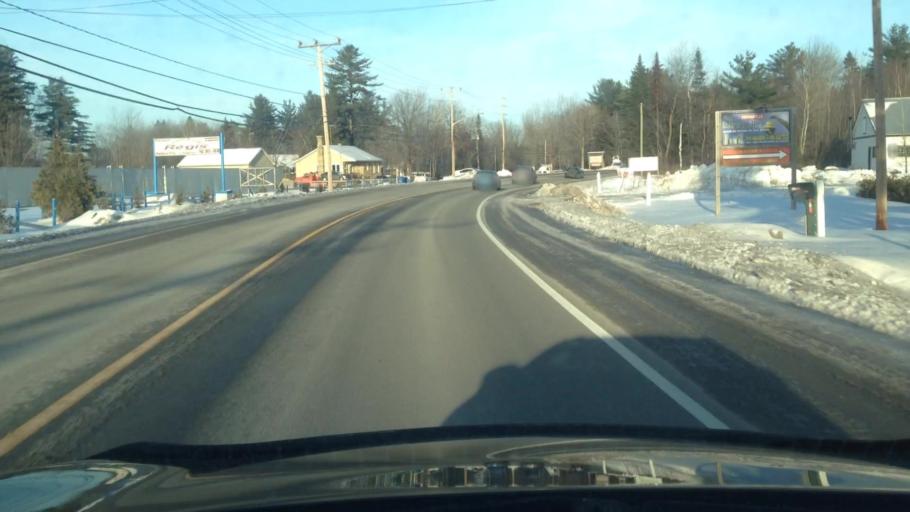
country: CA
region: Quebec
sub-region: Laurentides
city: Sainte-Sophie
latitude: 45.8146
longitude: -73.9138
